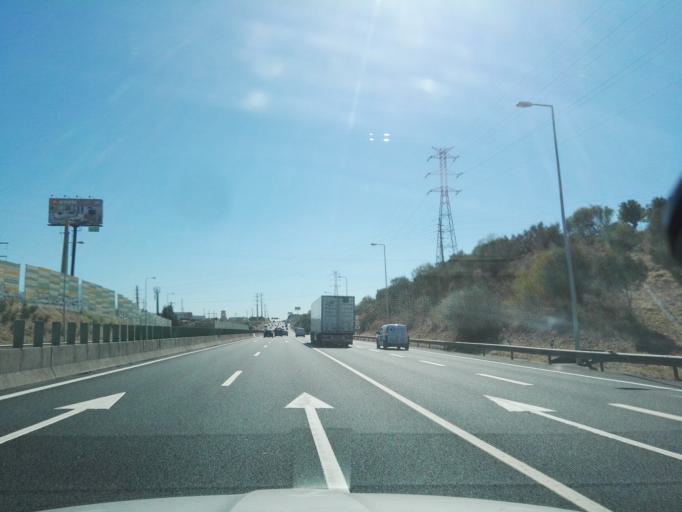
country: PT
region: Lisbon
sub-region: Loures
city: Santa Iria da Azoia
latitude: 38.8525
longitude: -9.0860
